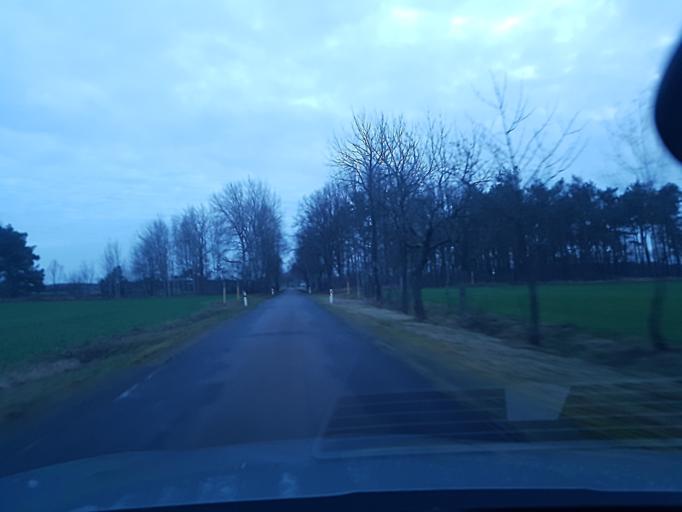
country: DE
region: Brandenburg
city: Finsterwalde
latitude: 51.6141
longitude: 13.6710
